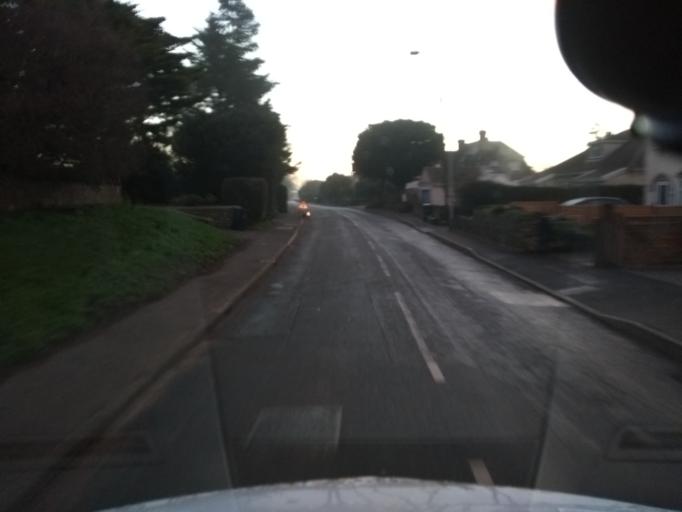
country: GB
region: England
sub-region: Somerset
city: Bridgwater
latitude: 51.1228
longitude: -3.0287
